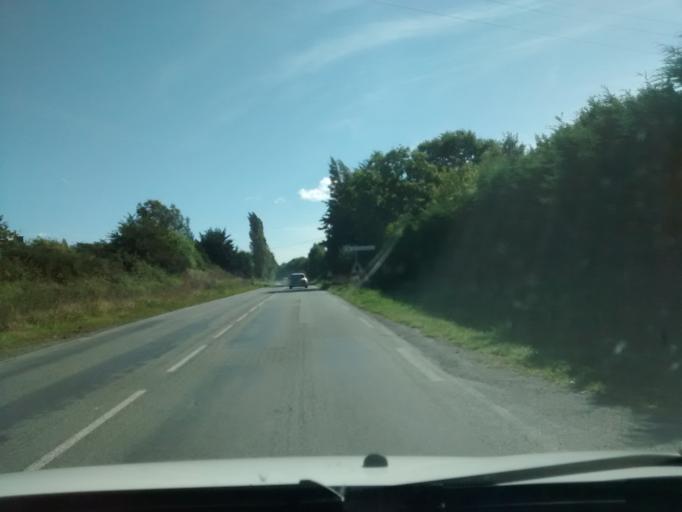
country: FR
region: Brittany
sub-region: Departement d'Ille-et-Vilaine
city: Saint-Briac-sur-Mer
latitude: 48.6159
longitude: -2.1211
